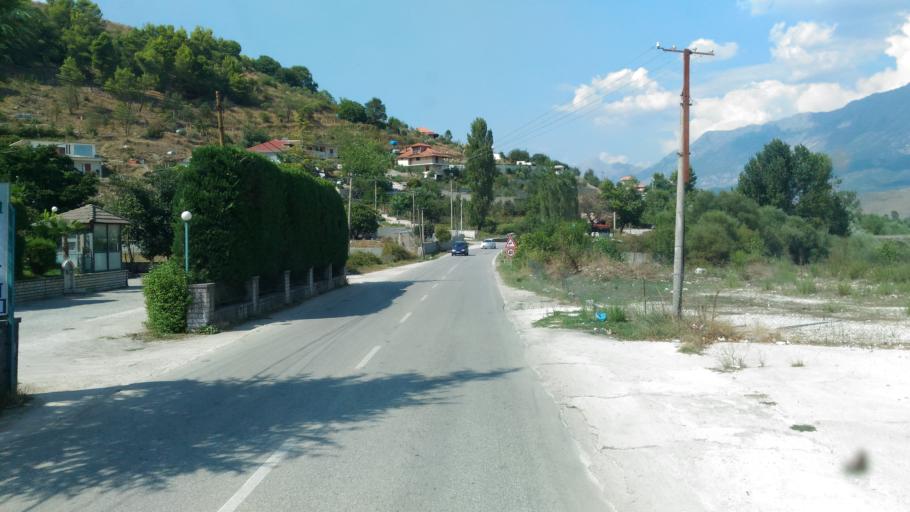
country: AL
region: Gjirokaster
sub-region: Rrethi i Gjirokastres
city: Dervician
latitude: 40.0586
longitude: 20.1724
